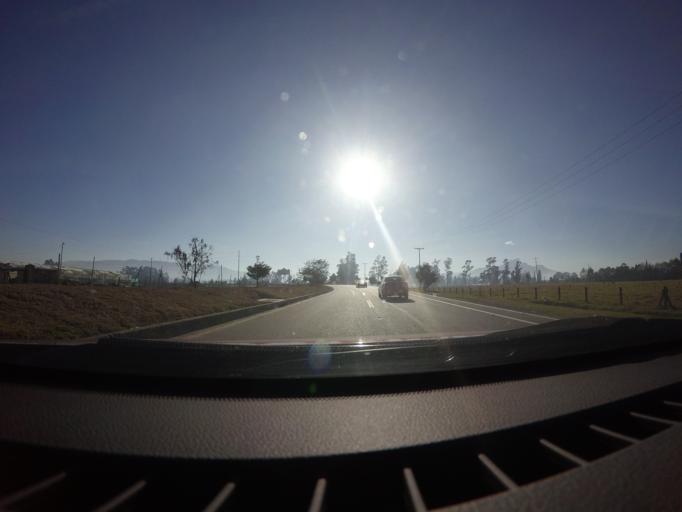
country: CO
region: Cundinamarca
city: Zipaquira
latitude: 4.9947
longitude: -73.9927
